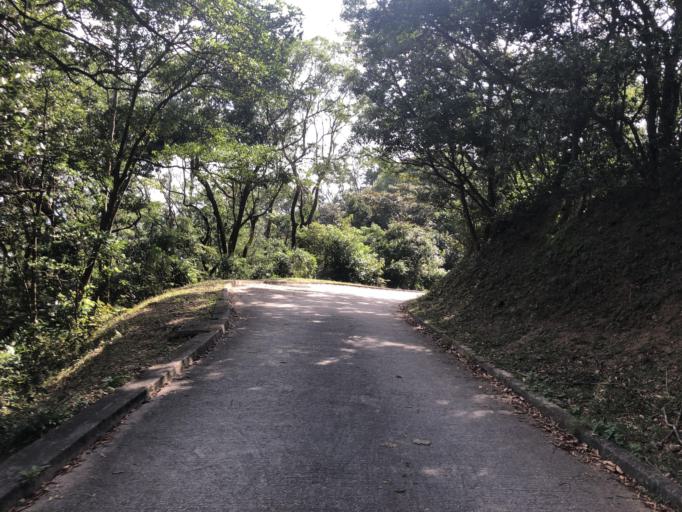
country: HK
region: Tsuen Wan
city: Tsuen Wan
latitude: 22.4066
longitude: 114.1001
